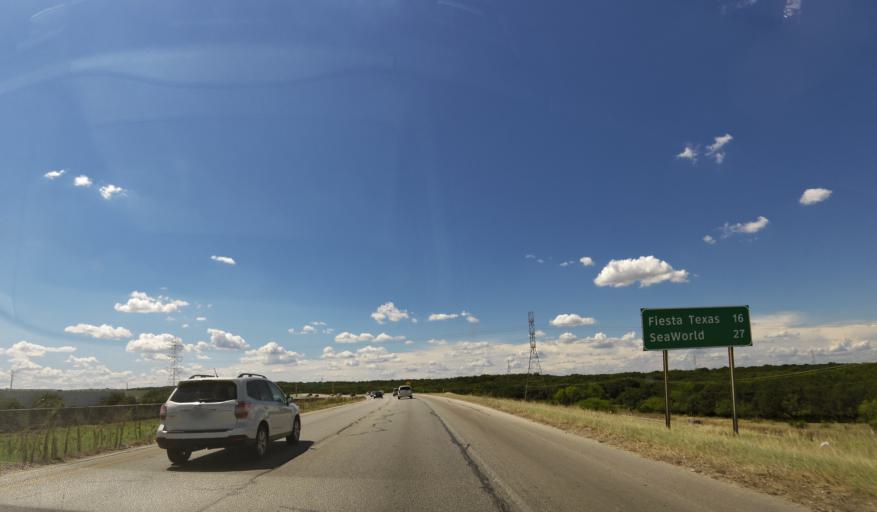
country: US
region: Texas
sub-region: Bexar County
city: Live Oak
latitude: 29.6002
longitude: -98.3576
